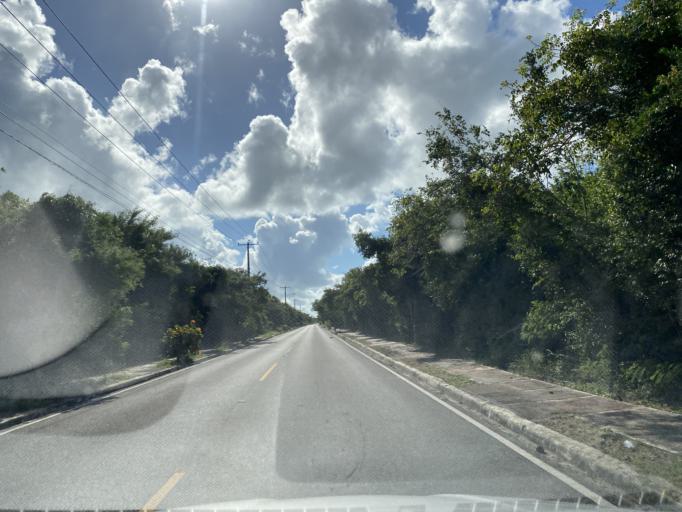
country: DO
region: La Altagracia
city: San Rafael del Yuma
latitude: 18.3398
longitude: -68.8119
